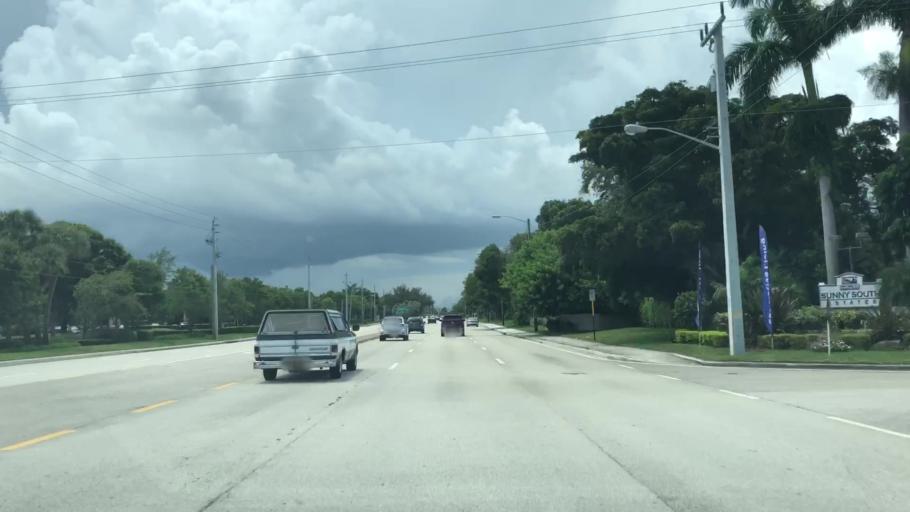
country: US
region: Florida
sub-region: Palm Beach County
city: Seminole Manor
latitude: 26.5465
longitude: -80.1006
